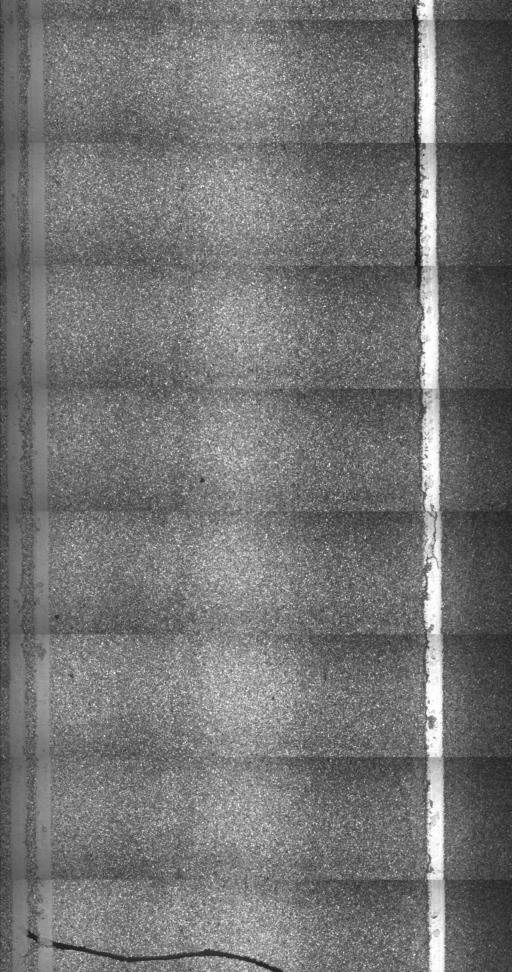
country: US
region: Vermont
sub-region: Bennington County
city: Manchester Center
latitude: 43.2351
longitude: -73.0833
